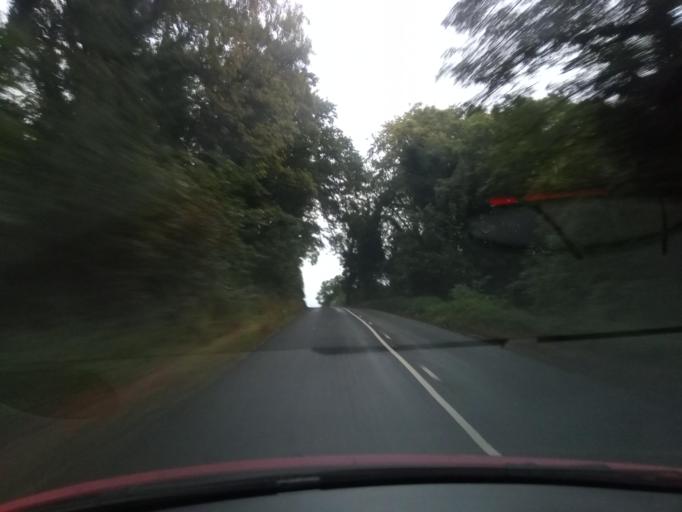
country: GB
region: England
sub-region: Darlington
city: Denton
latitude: 54.5741
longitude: -1.6777
